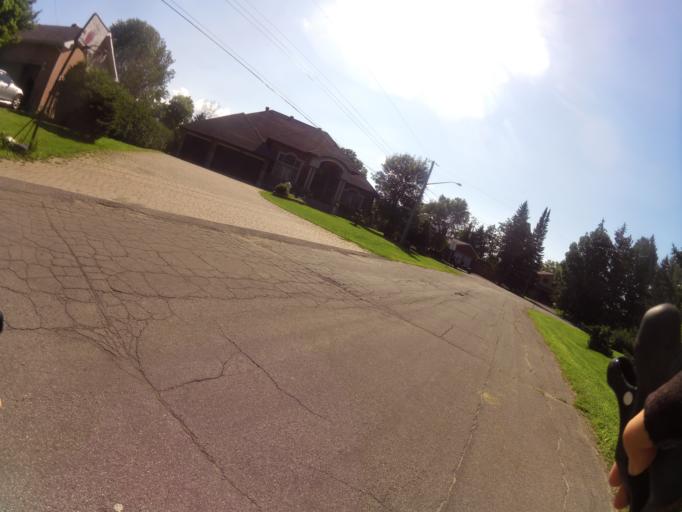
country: CA
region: Ontario
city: Ottawa
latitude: 45.3185
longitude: -75.6930
